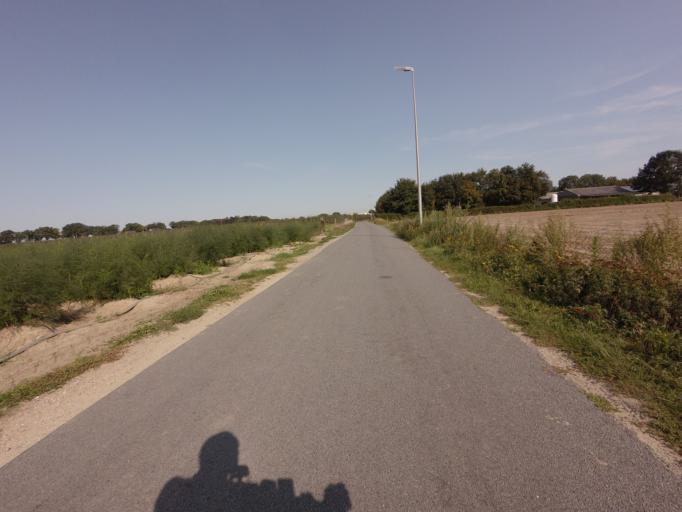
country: BE
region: Flanders
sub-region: Provincie Limburg
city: Maaseik
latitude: 51.1398
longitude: 5.8124
